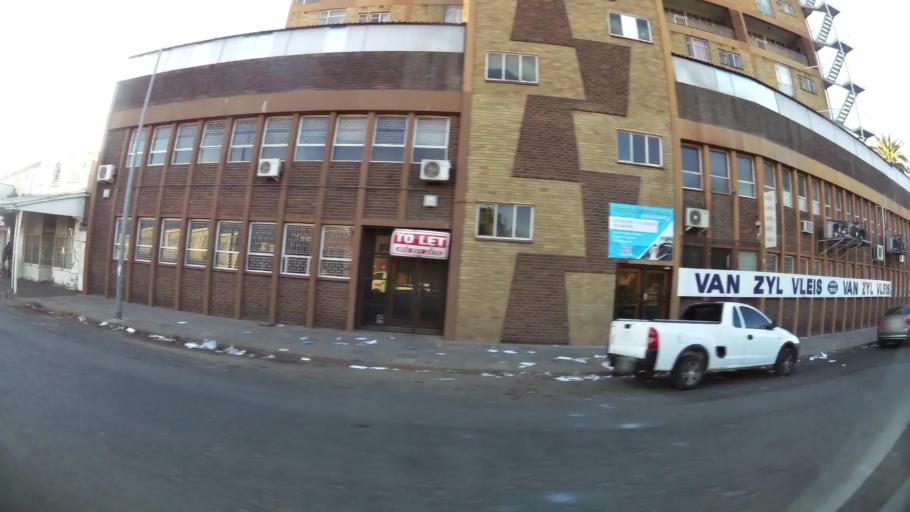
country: ZA
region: Northern Cape
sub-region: Frances Baard District Municipality
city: Kimberley
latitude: -28.7374
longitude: 24.7691
